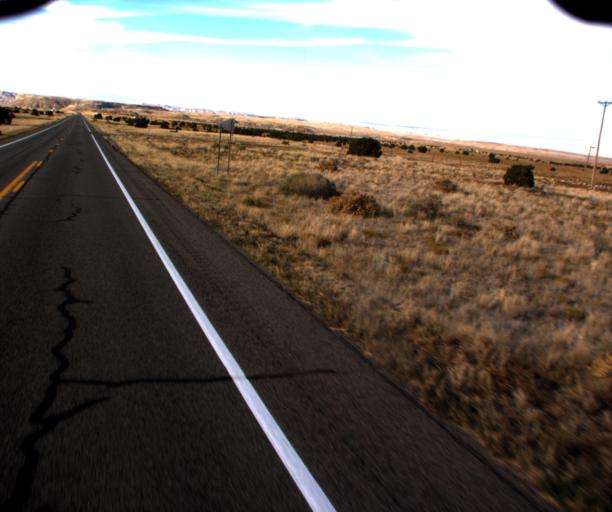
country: US
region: New Mexico
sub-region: San Juan County
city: Shiprock
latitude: 36.8962
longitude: -109.0646
